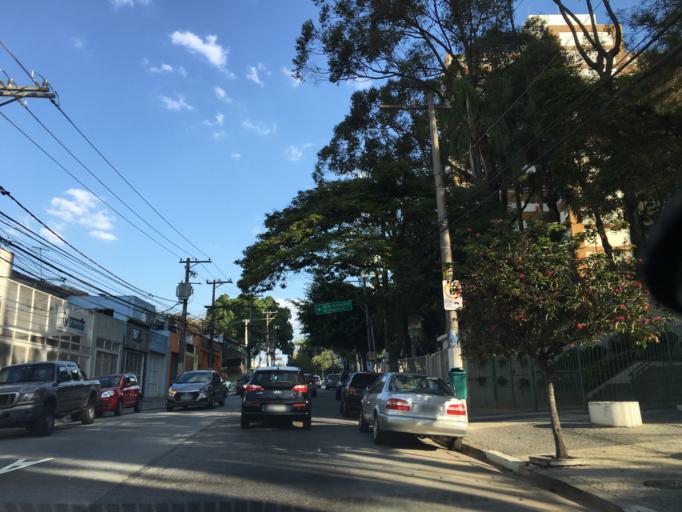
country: BR
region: Sao Paulo
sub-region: Sao Paulo
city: Sao Paulo
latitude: -23.4883
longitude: -46.6263
